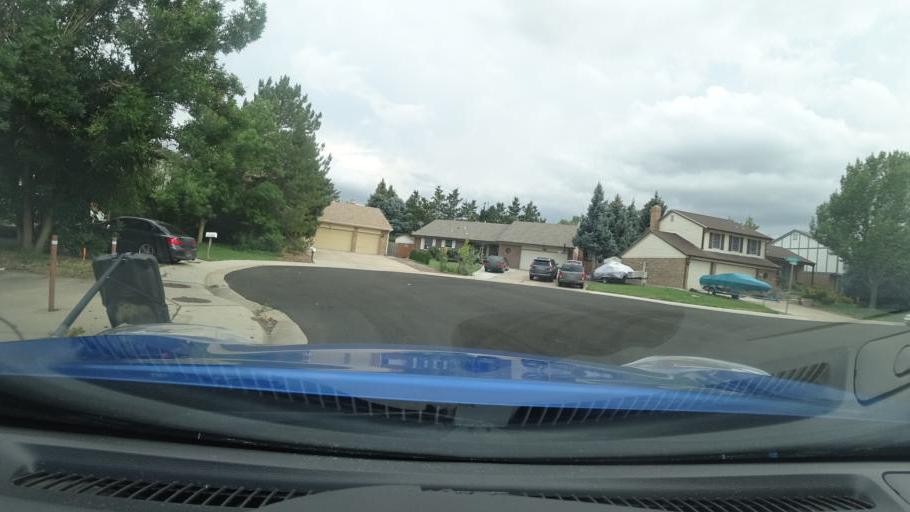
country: US
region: Colorado
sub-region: Adams County
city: Aurora
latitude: 39.6901
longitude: -104.8116
